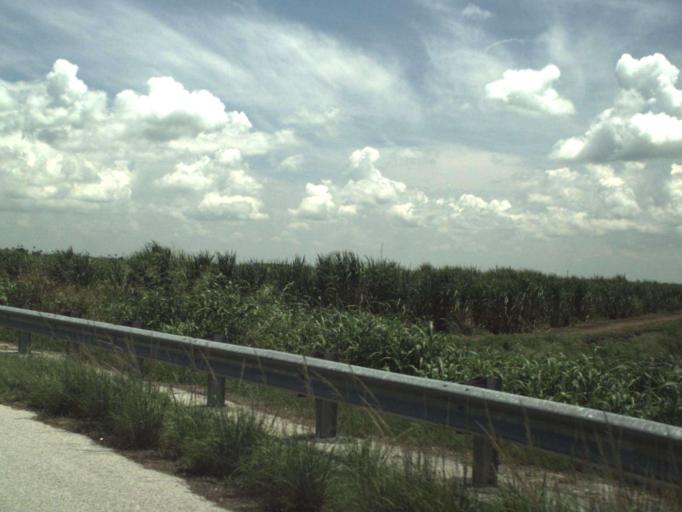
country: US
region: Florida
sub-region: Palm Beach County
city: Pahokee
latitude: 26.8603
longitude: -80.6285
